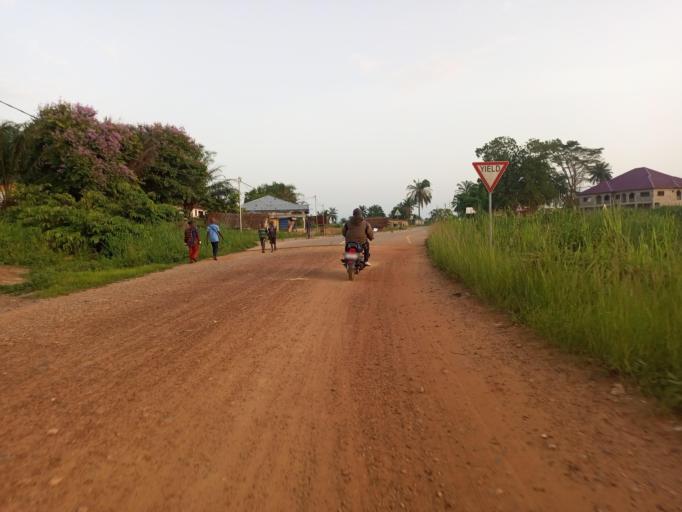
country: SL
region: Eastern Province
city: Pendembu
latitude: 8.0923
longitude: -10.6934
